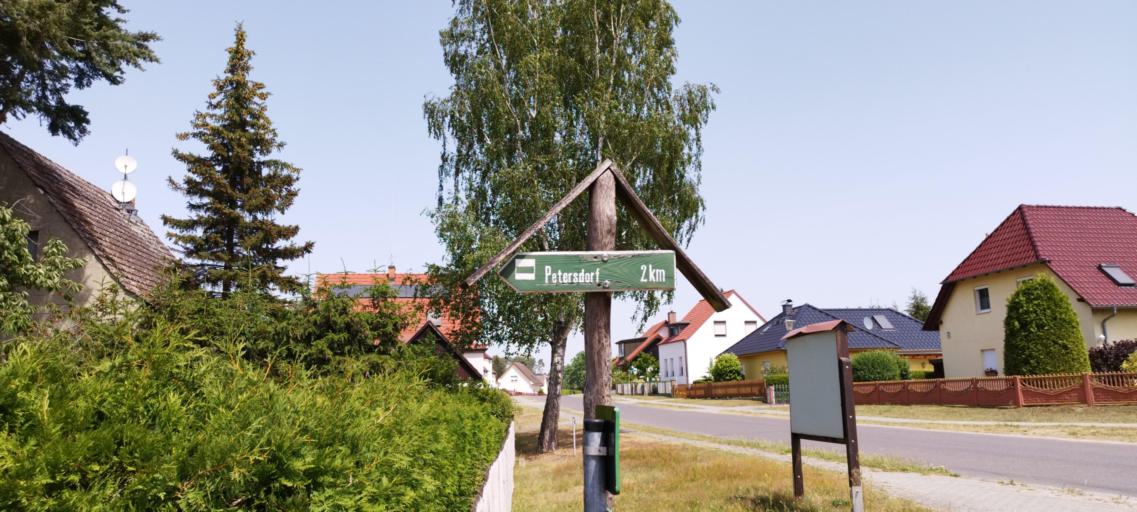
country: DE
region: Brandenburg
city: Bad Saarow
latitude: 52.3036
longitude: 14.0878
